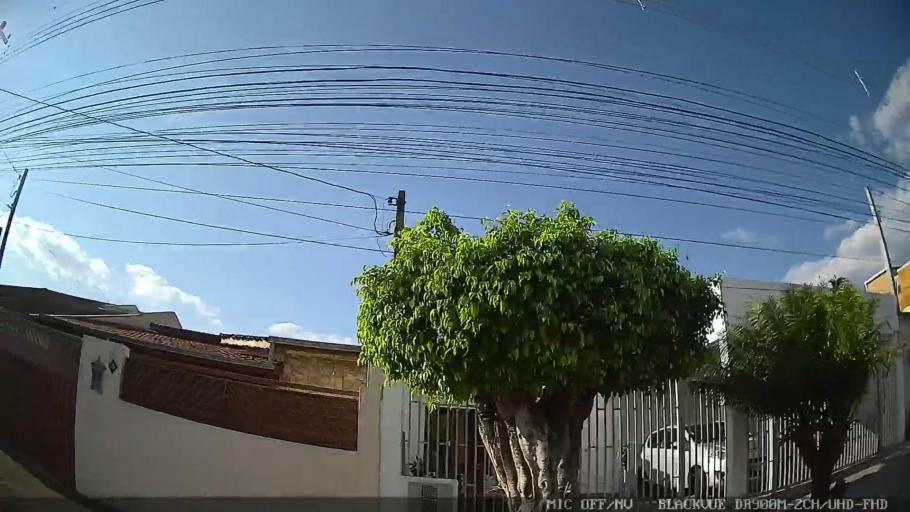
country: BR
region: Sao Paulo
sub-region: Cabreuva
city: Cabreuva
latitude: -23.2560
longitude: -47.0571
